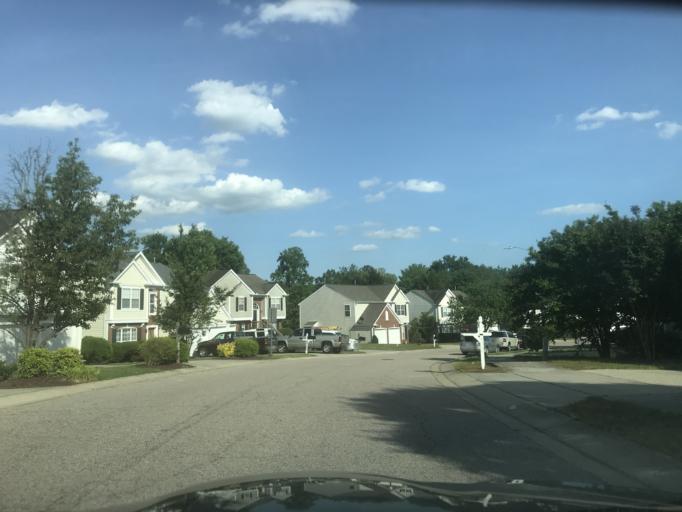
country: US
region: North Carolina
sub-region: Wake County
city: Knightdale
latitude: 35.8435
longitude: -78.5474
